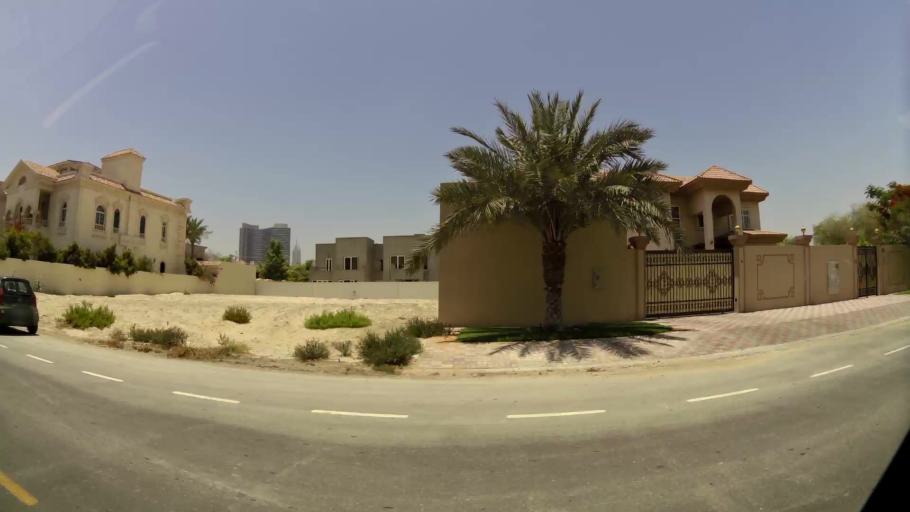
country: AE
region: Dubai
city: Dubai
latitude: 25.0953
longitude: 55.1905
